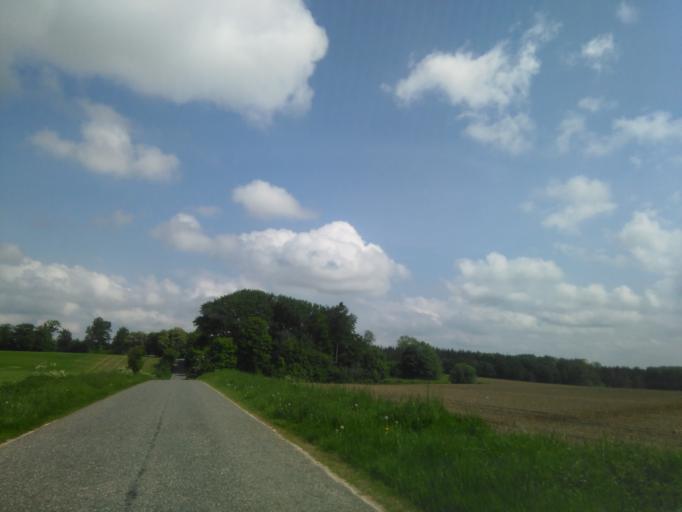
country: DK
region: Central Jutland
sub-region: Skanderborg Kommune
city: Galten
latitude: 56.2152
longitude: 9.9306
